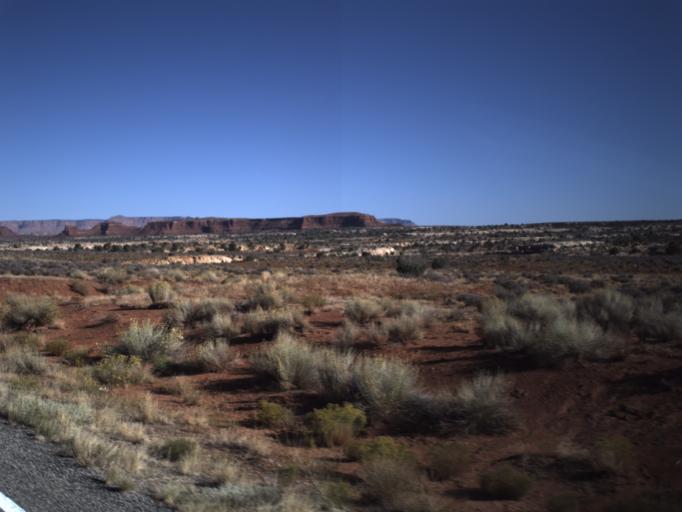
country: US
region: Utah
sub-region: San Juan County
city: Blanding
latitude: 37.7796
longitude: -110.2913
